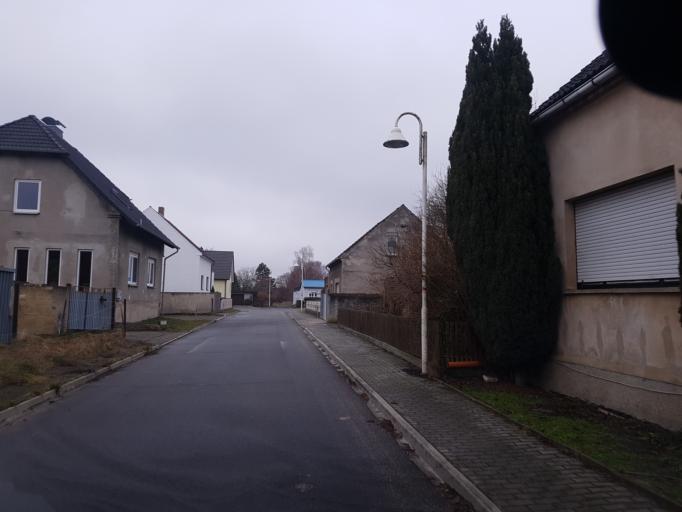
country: DE
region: Brandenburg
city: Plessa
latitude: 51.5333
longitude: 13.6217
